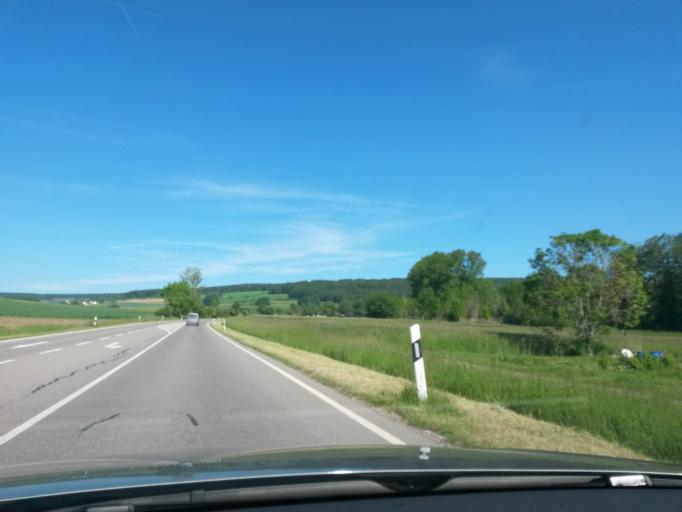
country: DE
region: Baden-Wuerttemberg
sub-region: Tuebingen Region
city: Altheim
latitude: 48.1646
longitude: 9.4546
